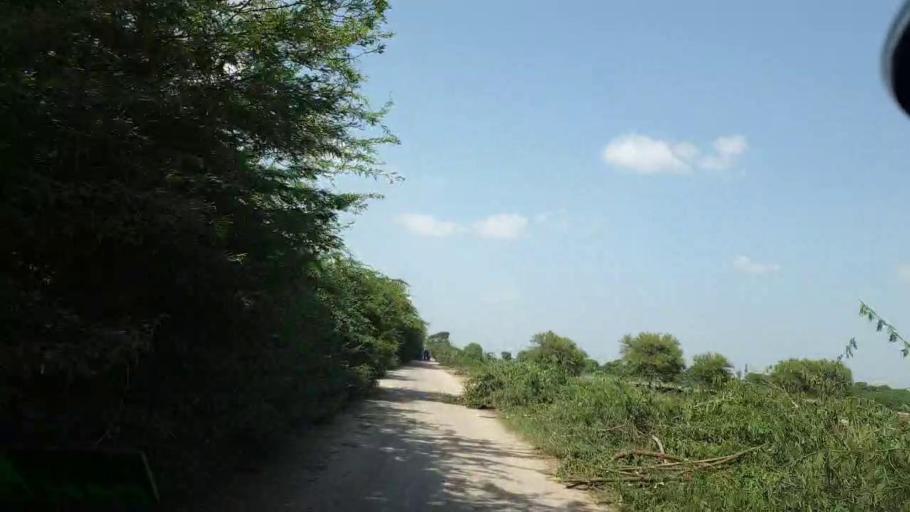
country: PK
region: Sindh
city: Kadhan
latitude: 24.6321
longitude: 69.2272
